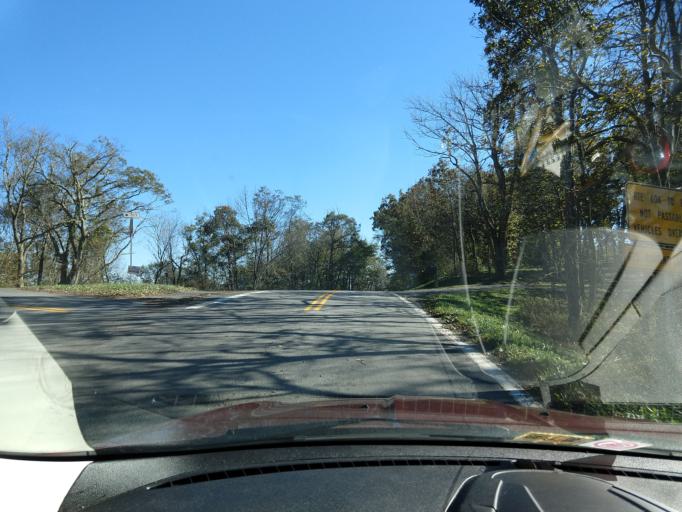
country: US
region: Virginia
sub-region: Alleghany County
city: Clifton Forge
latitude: 37.8758
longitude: -79.8878
